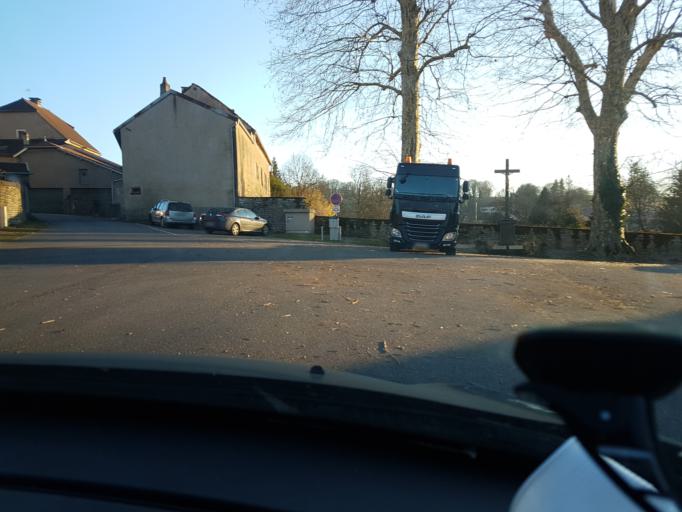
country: FR
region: Franche-Comte
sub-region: Departement de la Haute-Saone
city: Faverney
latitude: 47.9229
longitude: 6.0959
